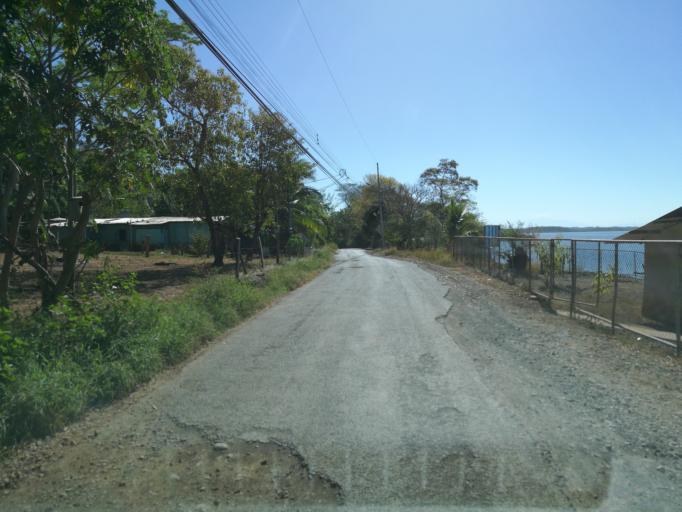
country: CR
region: Puntarenas
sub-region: Canton Central de Puntarenas
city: Puntarenas
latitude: 10.0956
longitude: -84.9819
